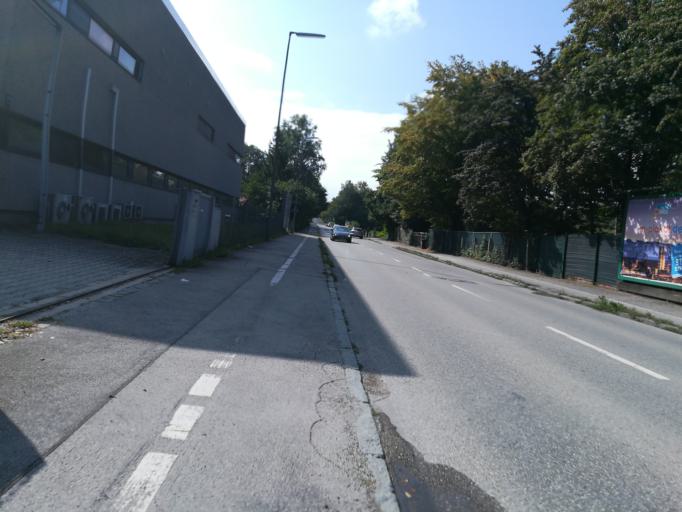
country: DE
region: Bavaria
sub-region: Upper Bavaria
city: Karlsfeld
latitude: 48.1952
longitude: 11.5238
